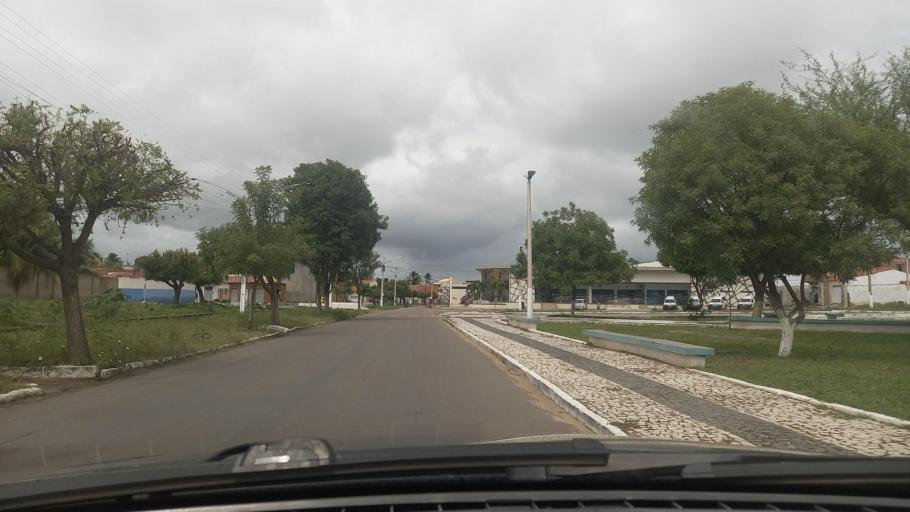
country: BR
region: Alagoas
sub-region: Delmiro Gouveia
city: Delmiro Gouveia
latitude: -9.3870
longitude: -38.0015
